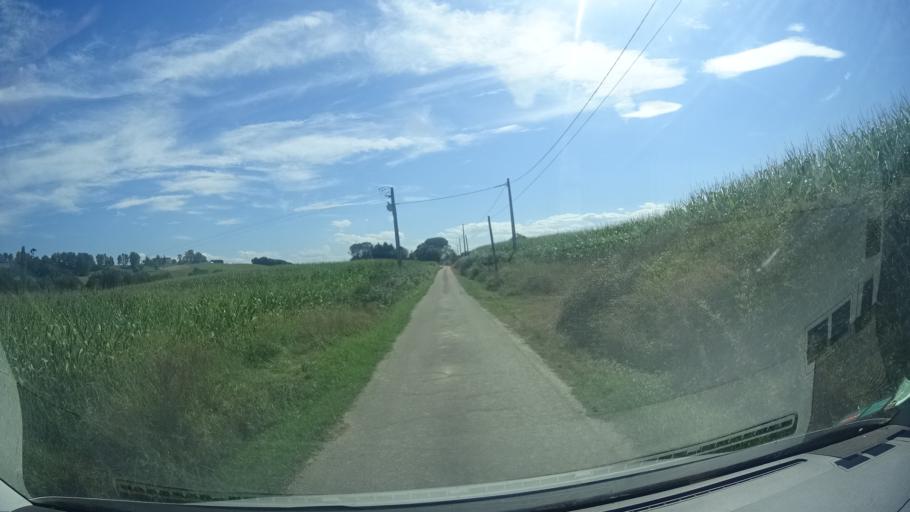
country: FR
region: Aquitaine
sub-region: Departement des Pyrenees-Atlantiques
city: Orthez
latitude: 43.4944
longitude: -0.7091
